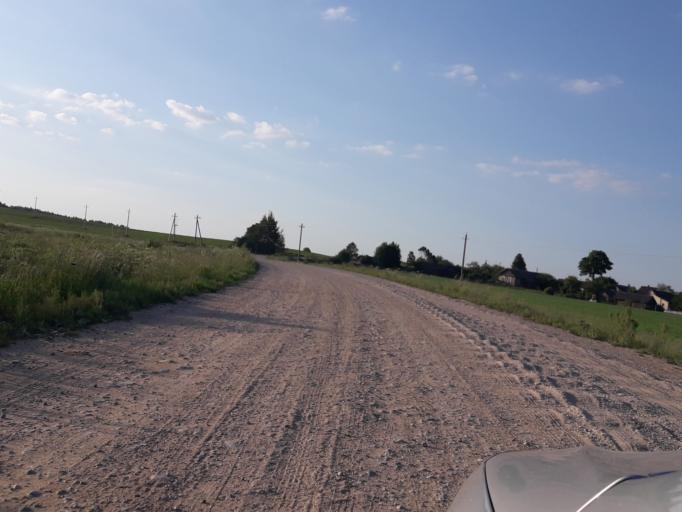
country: BY
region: Minsk
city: Radashkovichy
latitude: 54.1388
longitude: 27.1408
